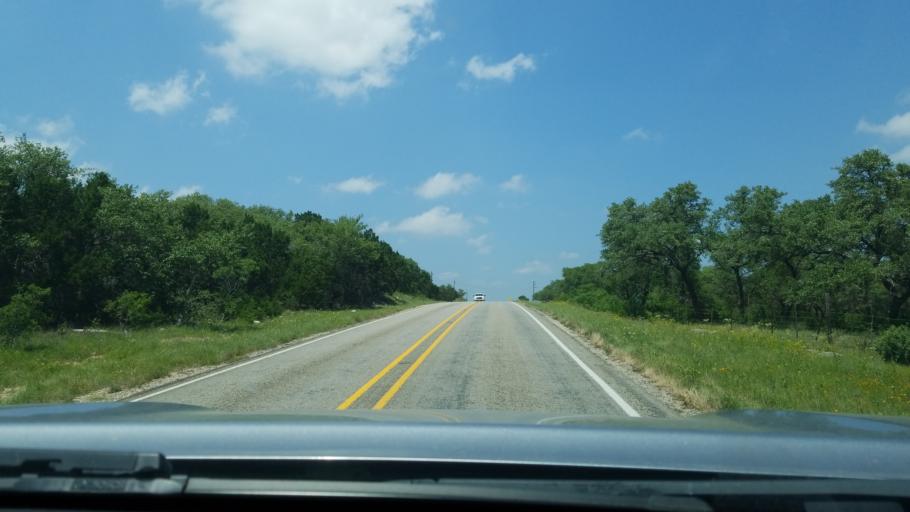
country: US
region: Texas
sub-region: Hays County
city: Woodcreek
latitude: 30.0722
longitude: -98.2205
